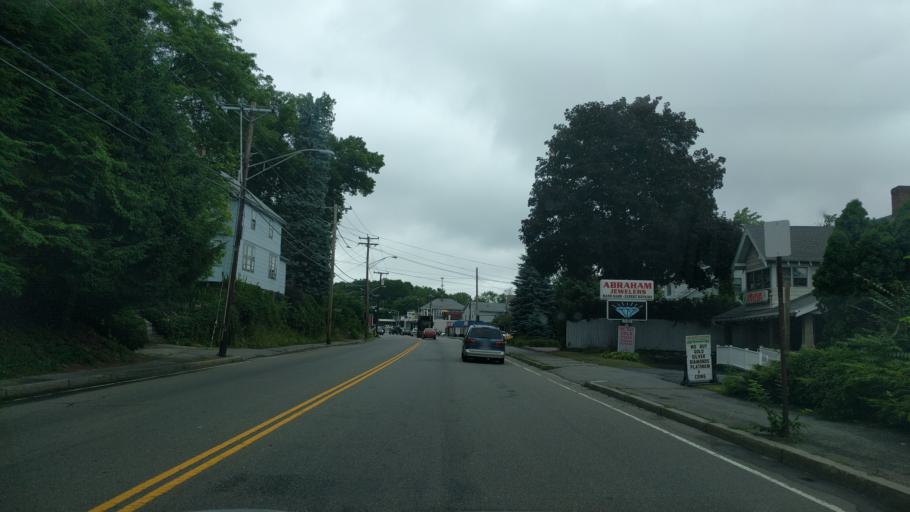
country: US
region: Massachusetts
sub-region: Worcester County
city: Sunderland
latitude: 42.2396
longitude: -71.7533
